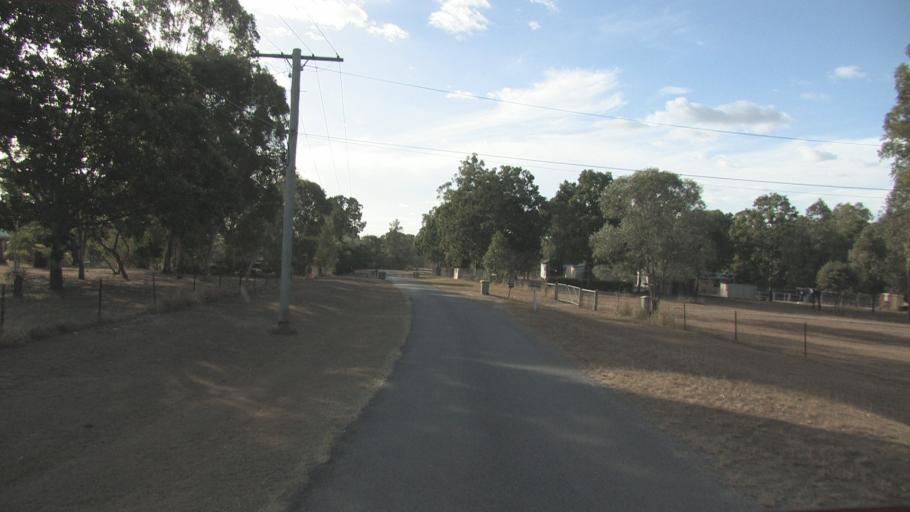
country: AU
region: Queensland
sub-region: Logan
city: Cedar Vale
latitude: -27.8791
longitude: 153.0210
